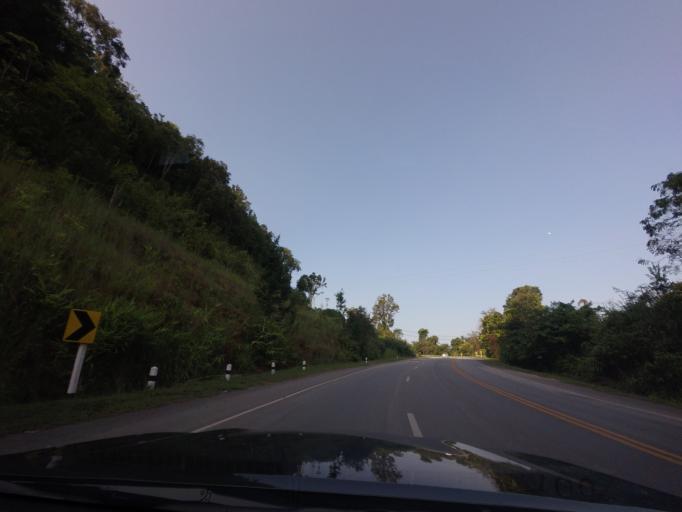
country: TH
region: Loei
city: Dan Sai
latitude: 17.2226
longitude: 101.1470
